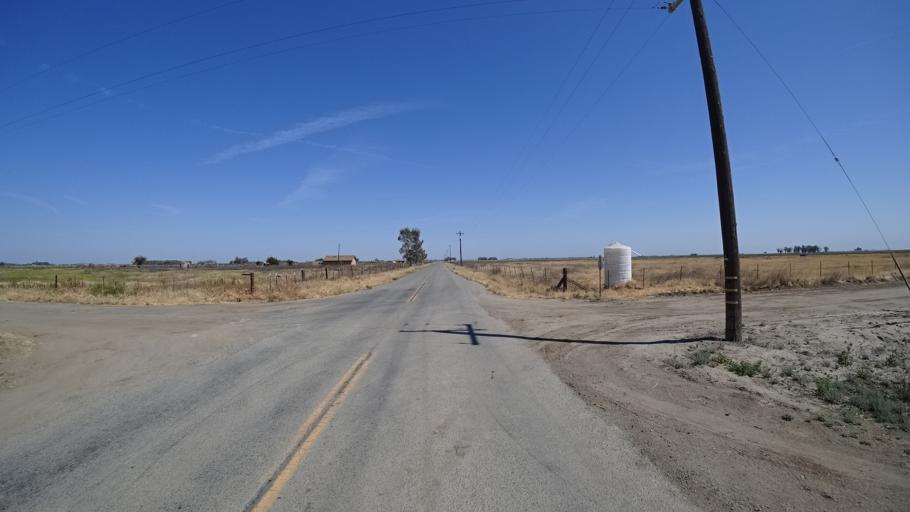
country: US
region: California
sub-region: Kings County
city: Stratford
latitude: 36.1746
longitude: -119.7803
